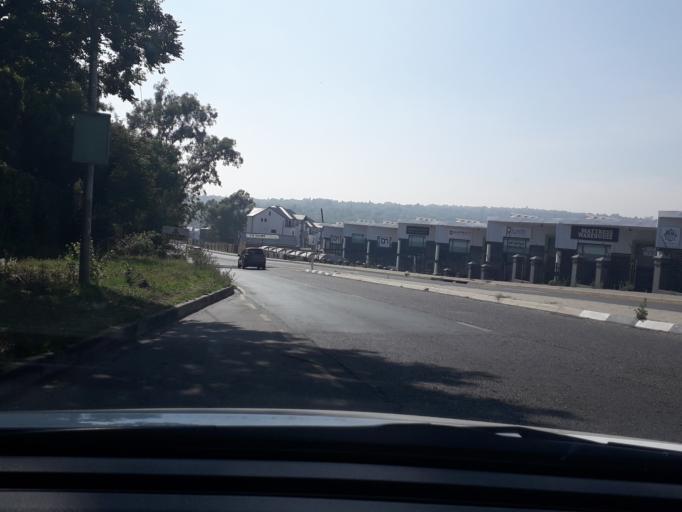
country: ZA
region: Gauteng
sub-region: City of Johannesburg Metropolitan Municipality
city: Diepsloot
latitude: -26.0590
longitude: 27.9741
